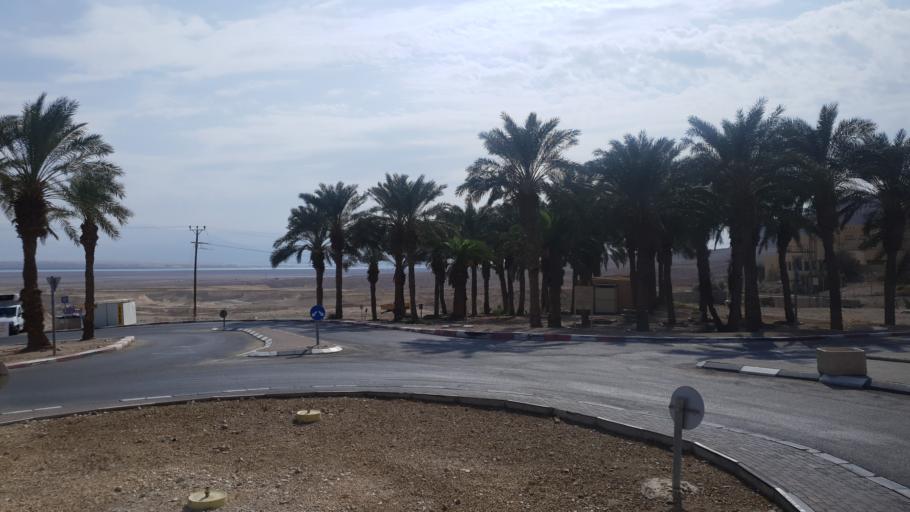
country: IL
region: Southern District
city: `En Boqeq
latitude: 31.3125
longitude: 35.3643
